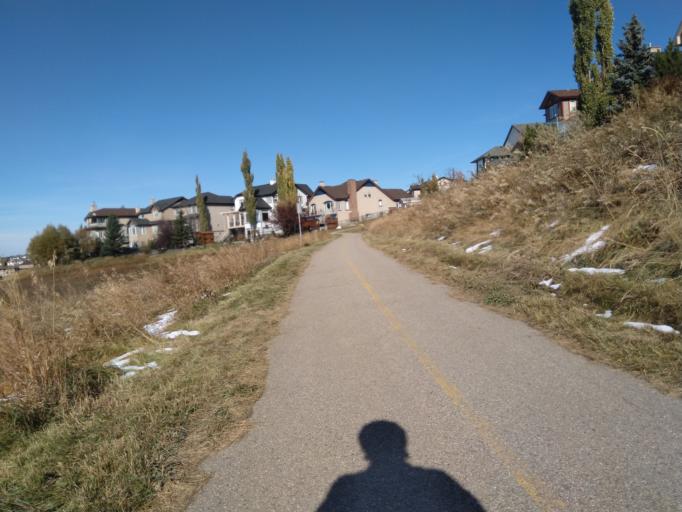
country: CA
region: Alberta
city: Calgary
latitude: 51.1566
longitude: -114.0962
